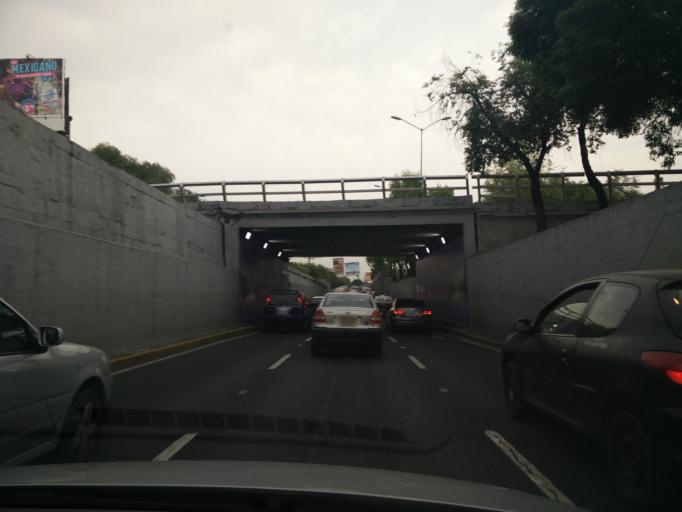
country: MX
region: Mexico City
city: Mexico City
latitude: 19.4050
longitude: -99.1213
